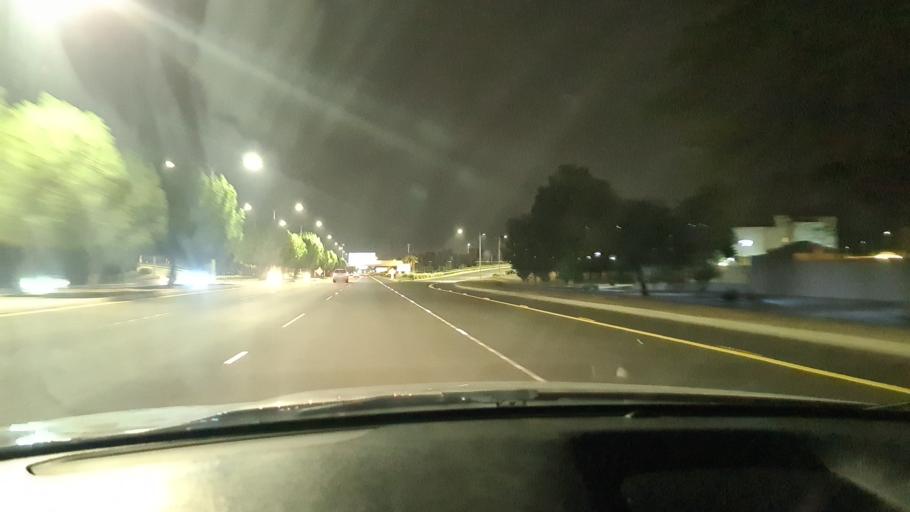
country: SA
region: Eastern Province
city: Al Jubayl
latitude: 27.1274
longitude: 49.5468
